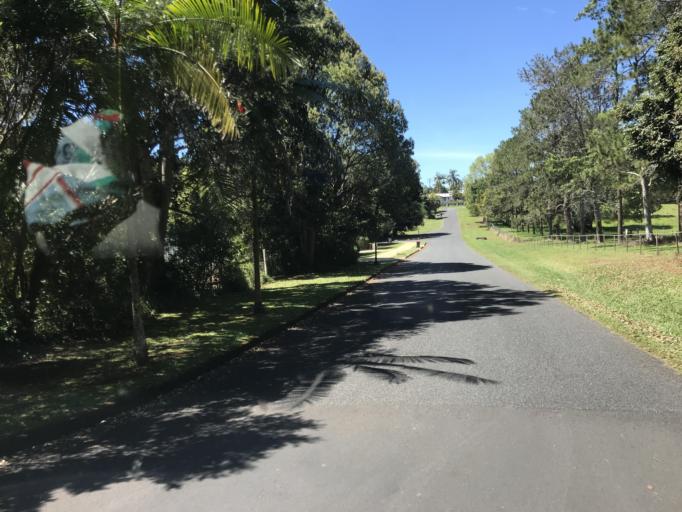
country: AU
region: Queensland
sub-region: Tablelands
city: Atherton
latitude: -17.3563
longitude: 145.5933
